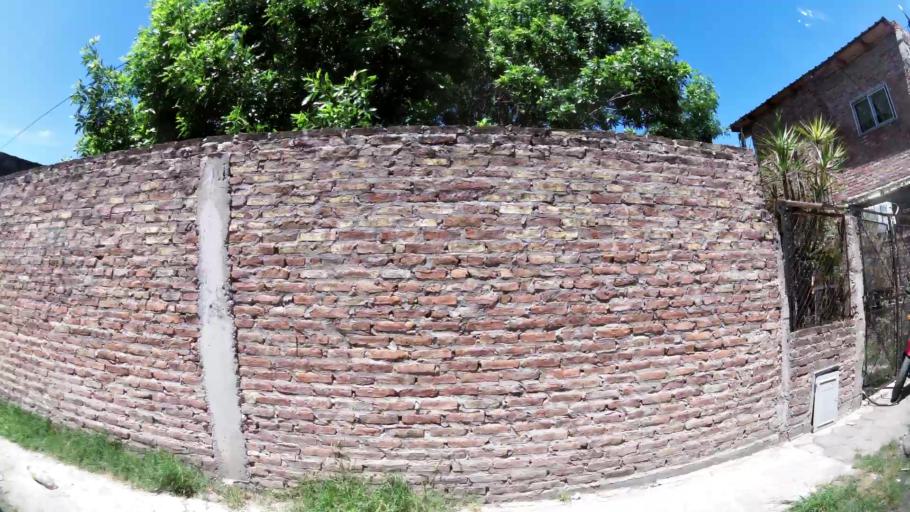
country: AR
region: Buenos Aires
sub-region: Partido de Quilmes
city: Quilmes
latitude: -34.7187
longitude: -58.3237
